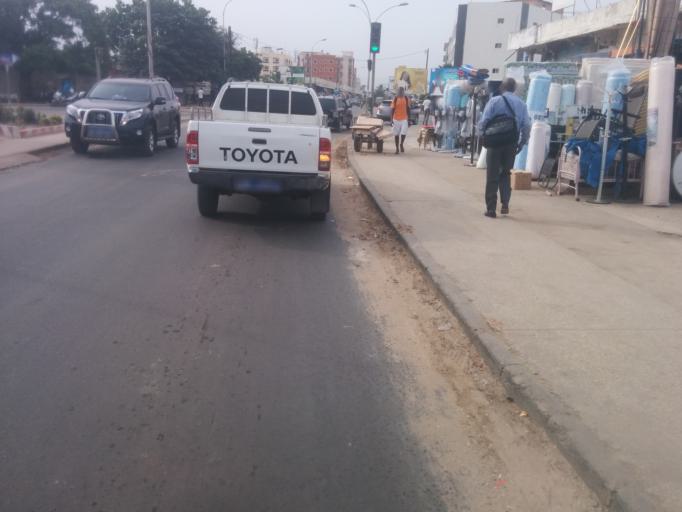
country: SN
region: Dakar
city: Grand Dakar
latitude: 14.7333
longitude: -17.4562
